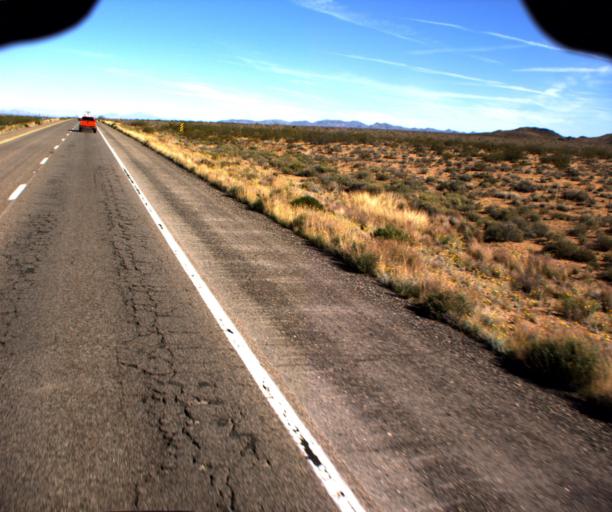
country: US
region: Arizona
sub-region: Mohave County
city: Dolan Springs
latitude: 35.4644
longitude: -114.3071
